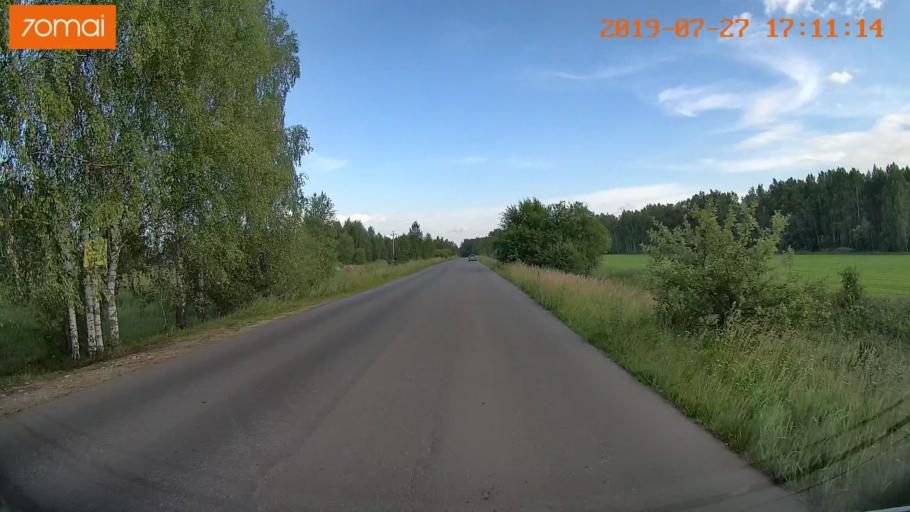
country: RU
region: Ivanovo
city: Novo-Talitsy
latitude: 57.0661
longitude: 40.8588
